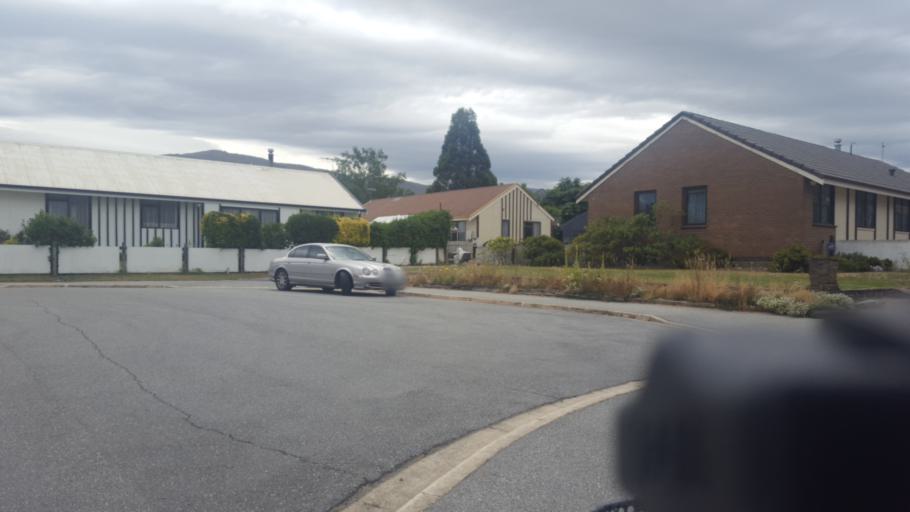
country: NZ
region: Otago
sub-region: Queenstown-Lakes District
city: Wanaka
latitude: -45.0446
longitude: 169.1841
